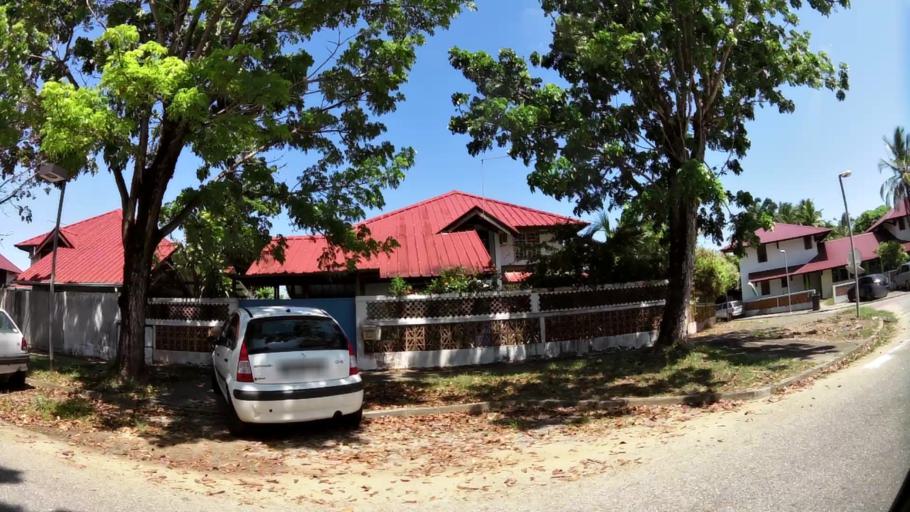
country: GF
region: Guyane
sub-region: Guyane
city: Kourou
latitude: 5.1750
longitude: -52.6474
